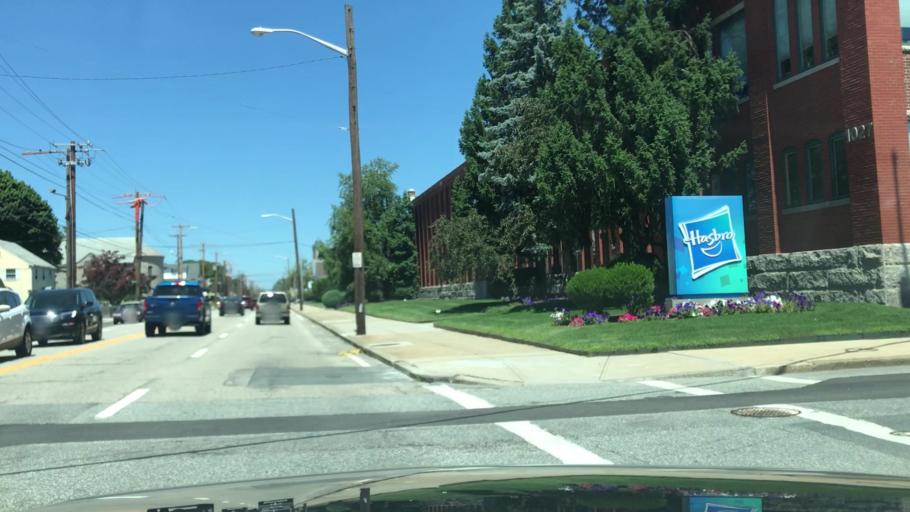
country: US
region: Massachusetts
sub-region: Bristol County
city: North Seekonk
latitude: 41.8822
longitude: -71.3539
